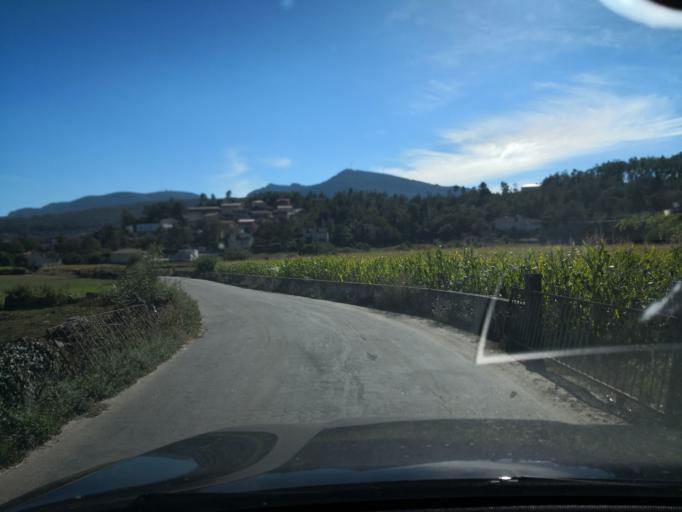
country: PT
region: Vila Real
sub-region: Santa Marta de Penaguiao
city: Santa Marta de Penaguiao
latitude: 41.2976
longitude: -7.8764
